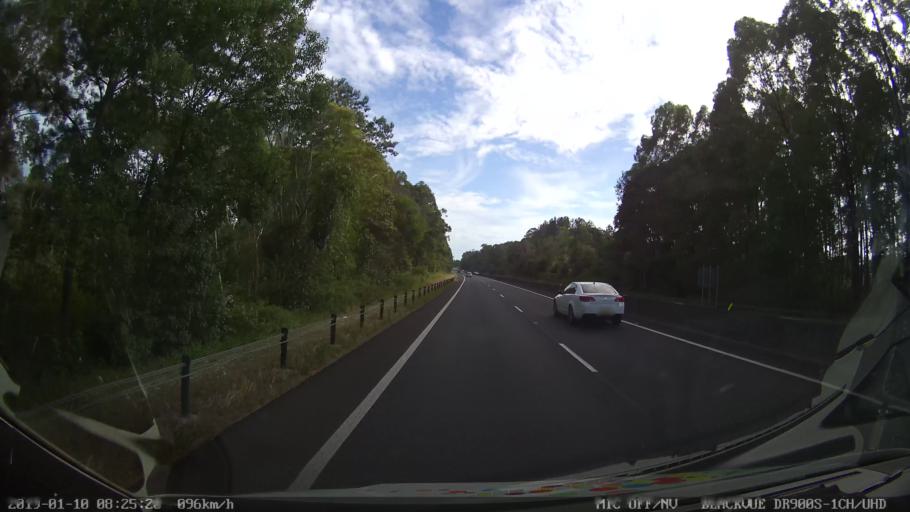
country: AU
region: New South Wales
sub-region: Coffs Harbour
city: Bonville
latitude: -30.4352
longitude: 153.0160
